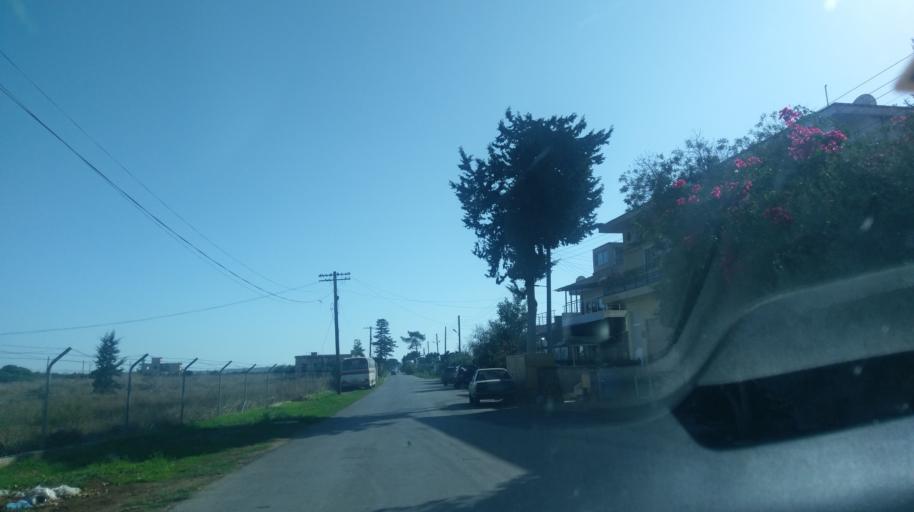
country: CY
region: Ammochostos
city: Famagusta
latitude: 35.0990
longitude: 33.9500
